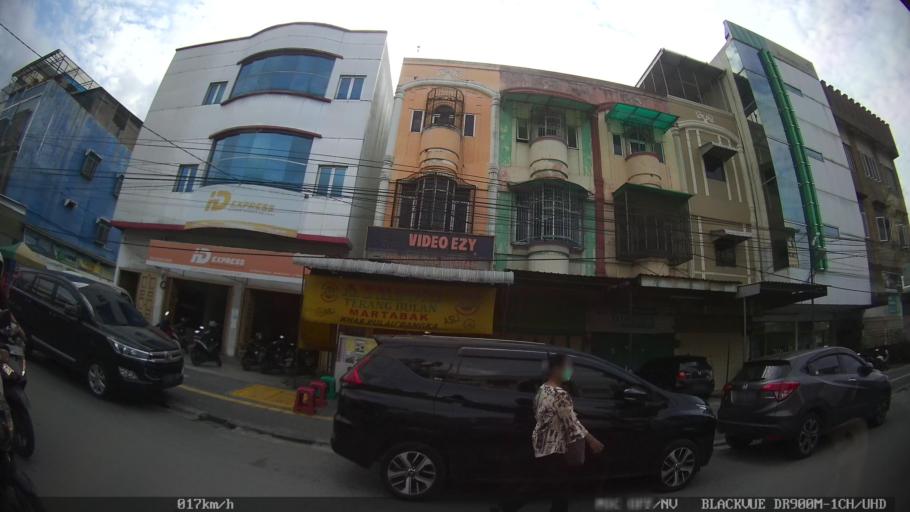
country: ID
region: North Sumatra
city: Medan
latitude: 3.6126
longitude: 98.6791
